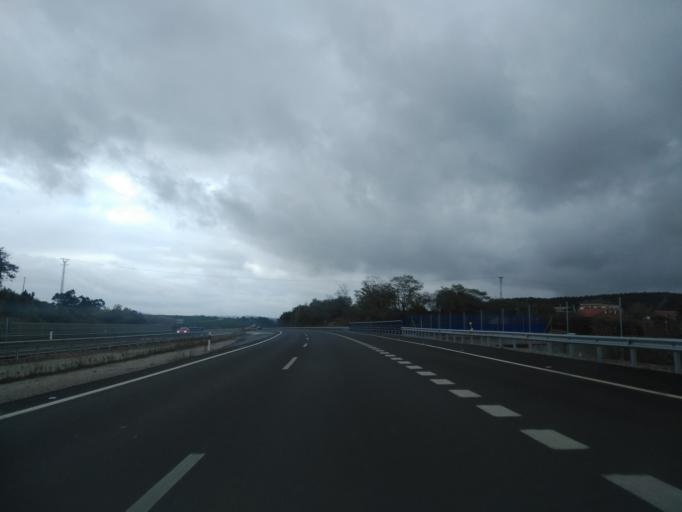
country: ES
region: Cantabria
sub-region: Provincia de Cantabria
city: Polanco
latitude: 43.3450
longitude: -3.9958
